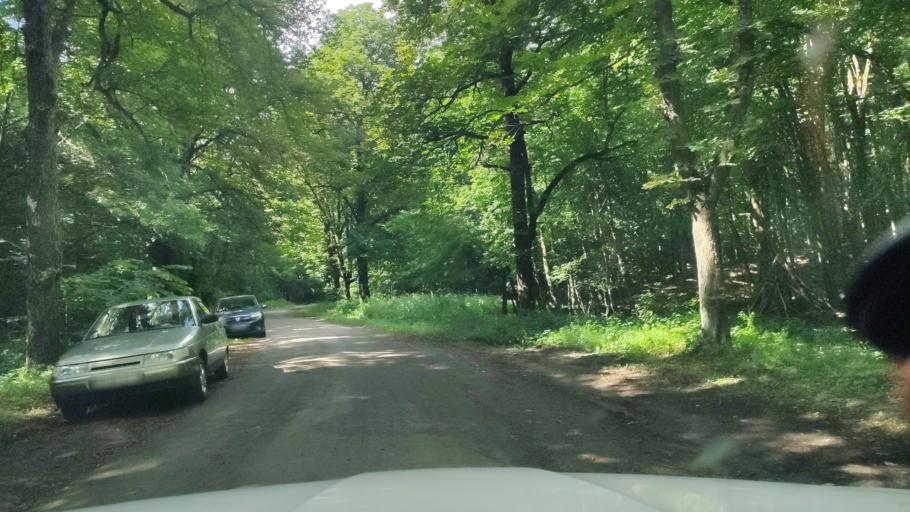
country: HU
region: Heves
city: Parad
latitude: 47.8991
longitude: 20.0567
